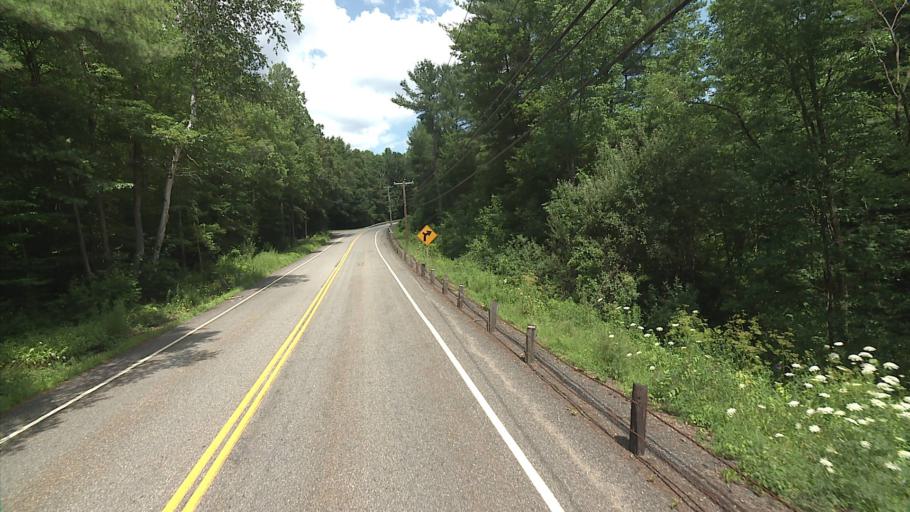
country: US
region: Connecticut
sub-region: Litchfield County
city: Winsted
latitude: 41.9903
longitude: -72.9982
